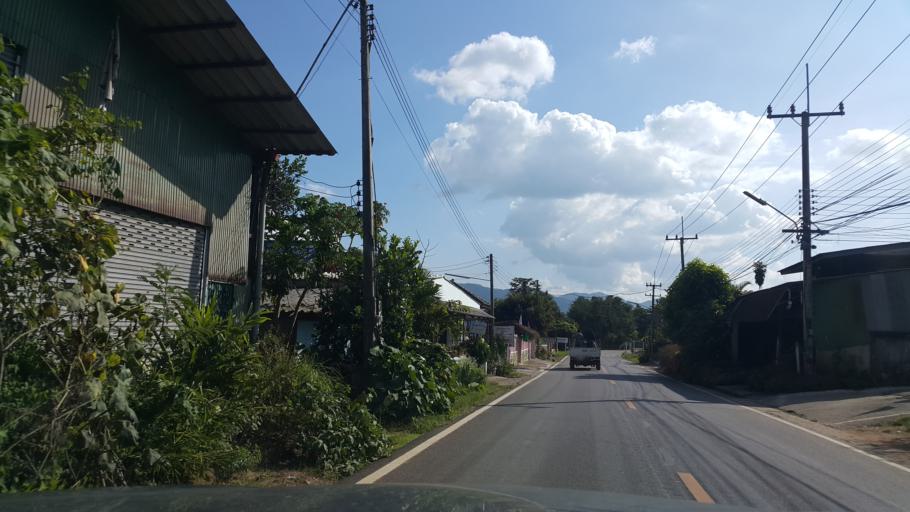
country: TH
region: Lamphun
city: Mae Tha
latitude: 18.5607
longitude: 99.2571
